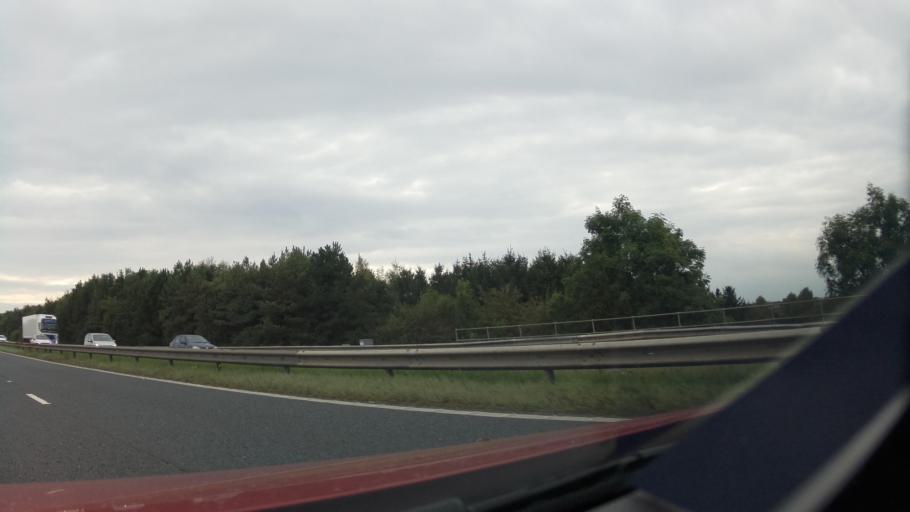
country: GB
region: England
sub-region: Darlington
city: Coatham Mundeville
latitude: 54.5661
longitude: -1.5835
